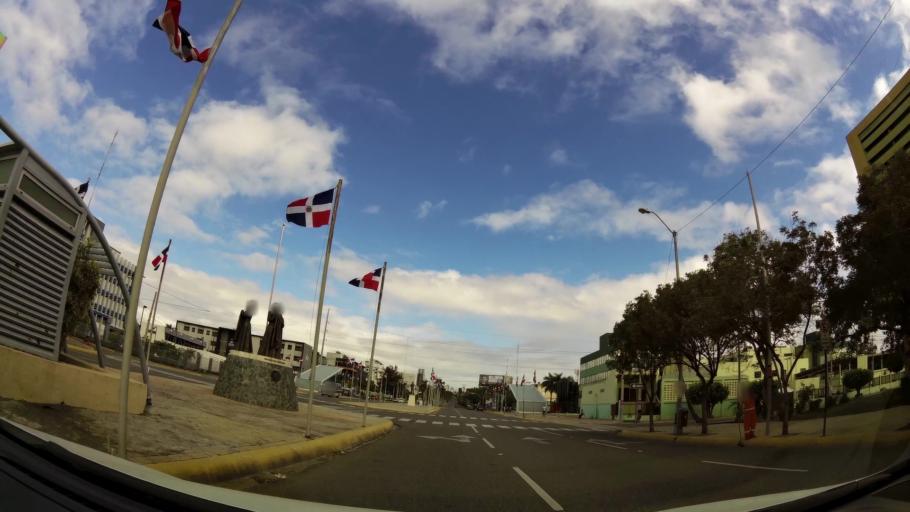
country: DO
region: Nacional
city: La Julia
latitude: 18.4500
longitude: -69.9268
